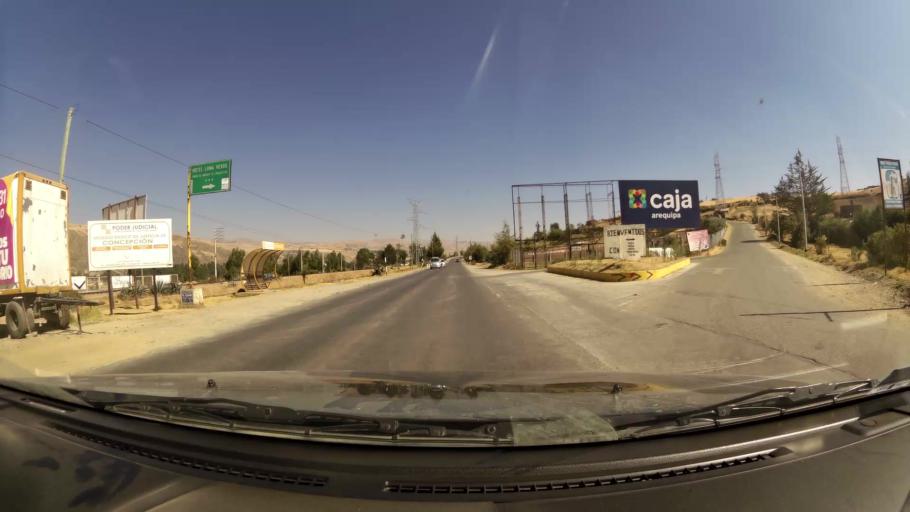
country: PE
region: Junin
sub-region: Provincia de Concepcion
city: Concepcion
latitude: -11.9381
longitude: -75.3099
